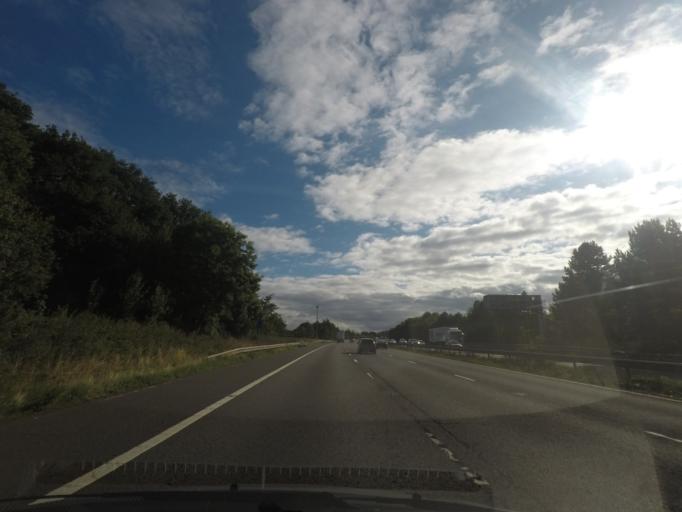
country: GB
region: England
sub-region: Leicestershire
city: Markfield
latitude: 52.7240
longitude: -1.2825
